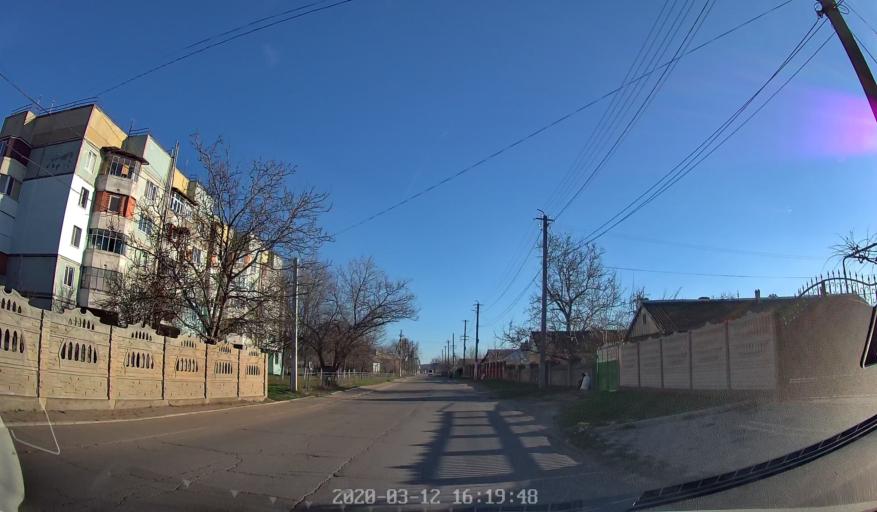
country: MD
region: Anenii Noi
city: Anenii Noi
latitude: 46.8819
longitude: 29.3054
